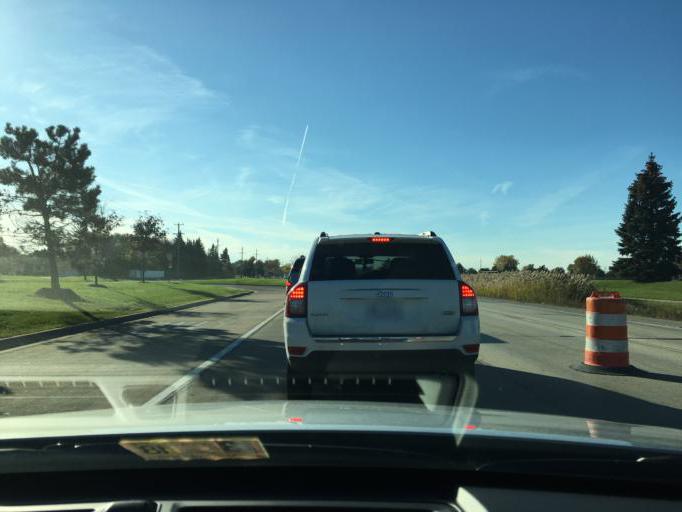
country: US
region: Michigan
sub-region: Macomb County
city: Sterling Heights
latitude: 42.5667
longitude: -83.0060
